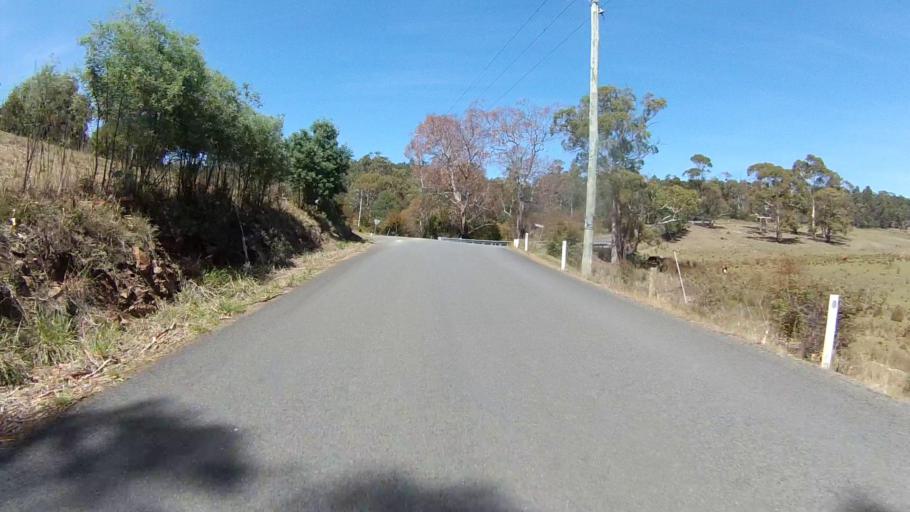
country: AU
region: Tasmania
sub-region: Sorell
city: Sorell
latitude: -42.7635
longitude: 147.6489
